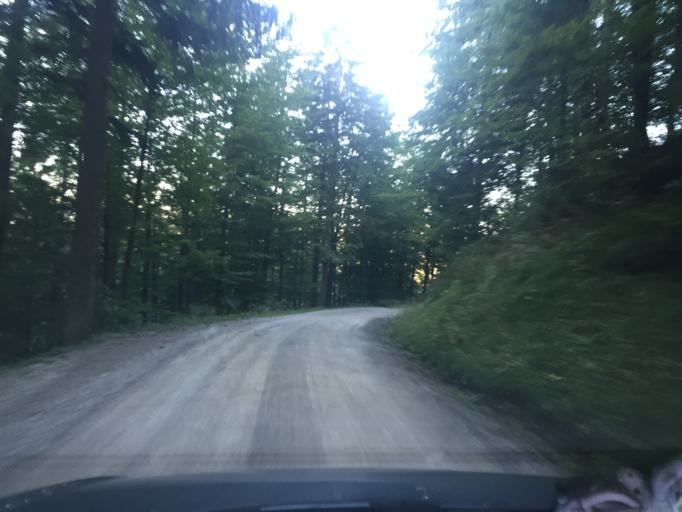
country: SI
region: Ravne na Koroskem
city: Kotlje
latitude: 46.4605
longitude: 14.9960
